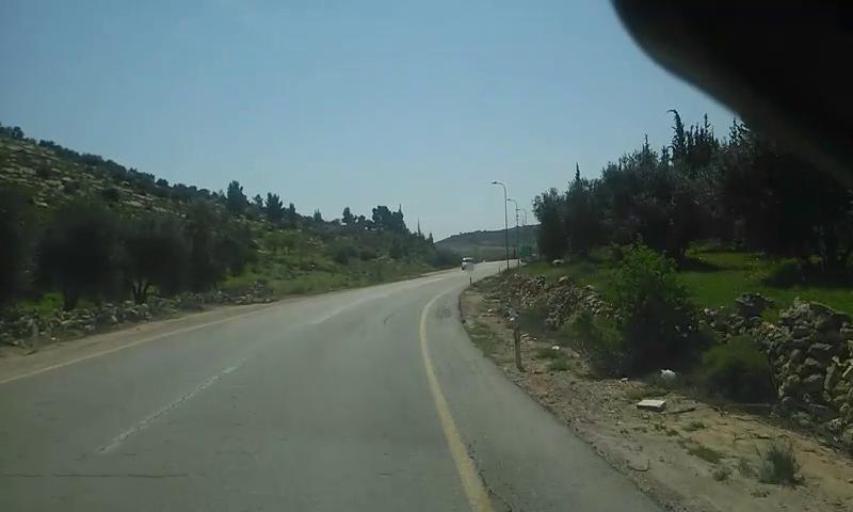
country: PS
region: West Bank
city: Karmah
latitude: 31.4461
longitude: 35.0214
